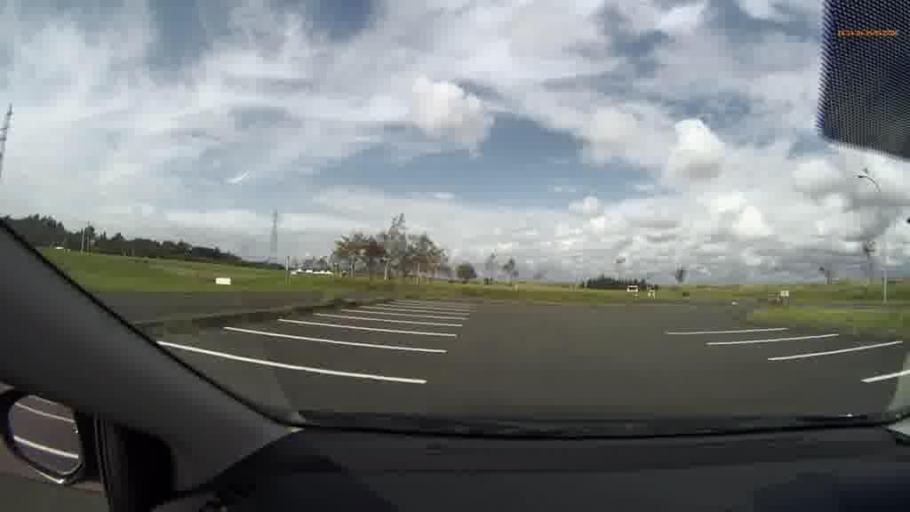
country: JP
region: Hokkaido
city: Kushiro
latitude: 43.0291
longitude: 144.4089
